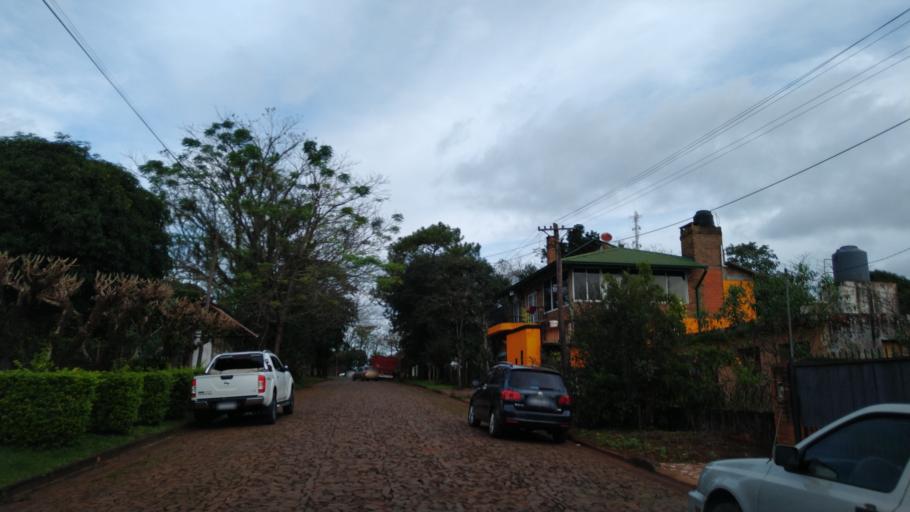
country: AR
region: Misiones
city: Jardin America
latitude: -27.0458
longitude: -55.2434
